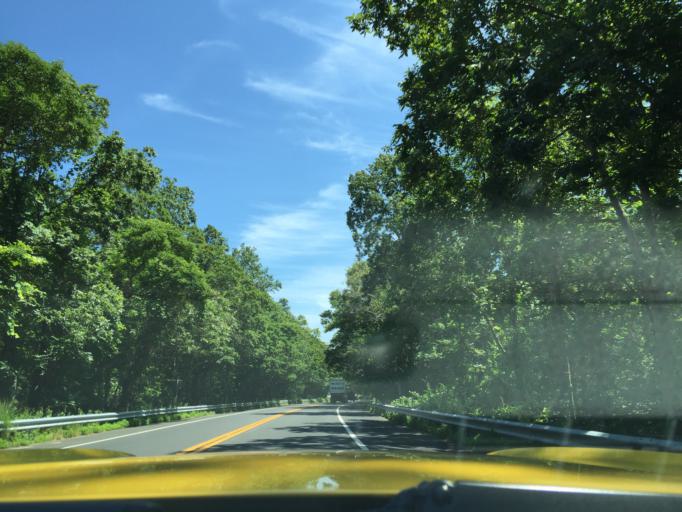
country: US
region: New York
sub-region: Suffolk County
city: Montauk
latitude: 41.0295
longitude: -71.9790
